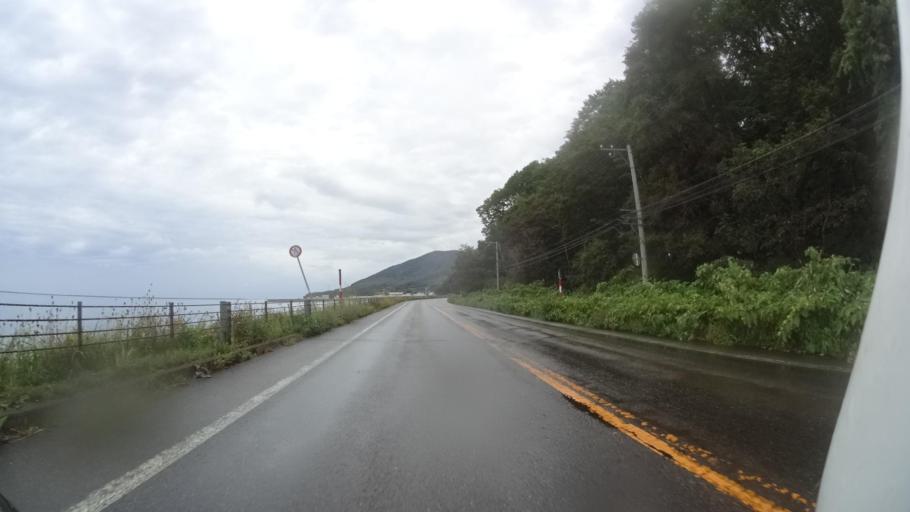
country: JP
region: Hokkaido
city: Kitami
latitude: 44.0960
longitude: 143.7946
